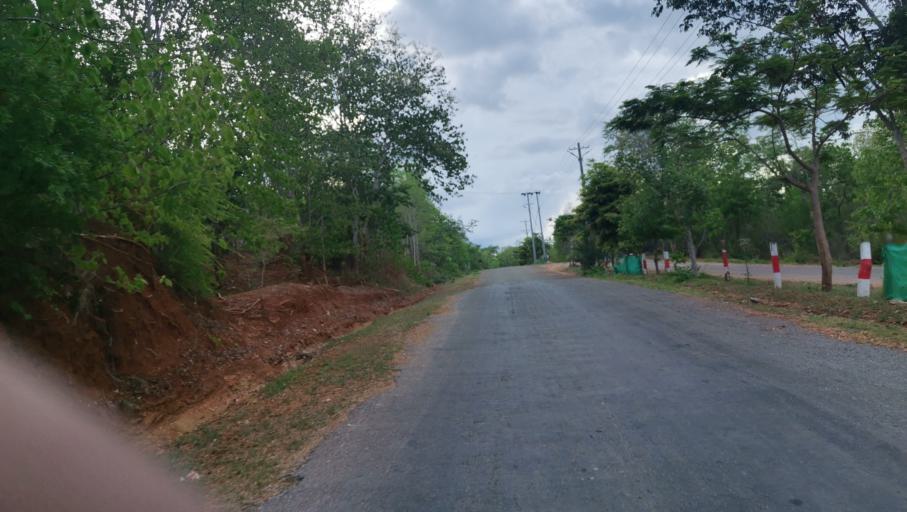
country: MM
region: Magway
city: Minbu
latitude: 20.0867
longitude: 94.5743
